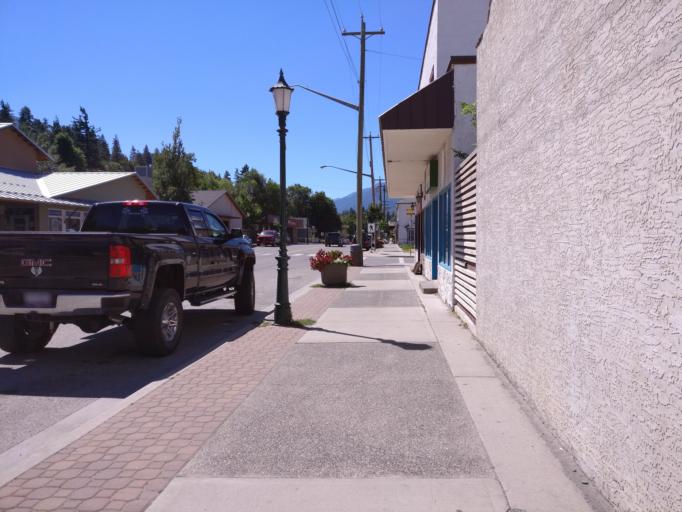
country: CA
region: British Columbia
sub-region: Thompson-Nicola Regional District
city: Ashcroft
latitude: 50.2323
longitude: -121.5811
